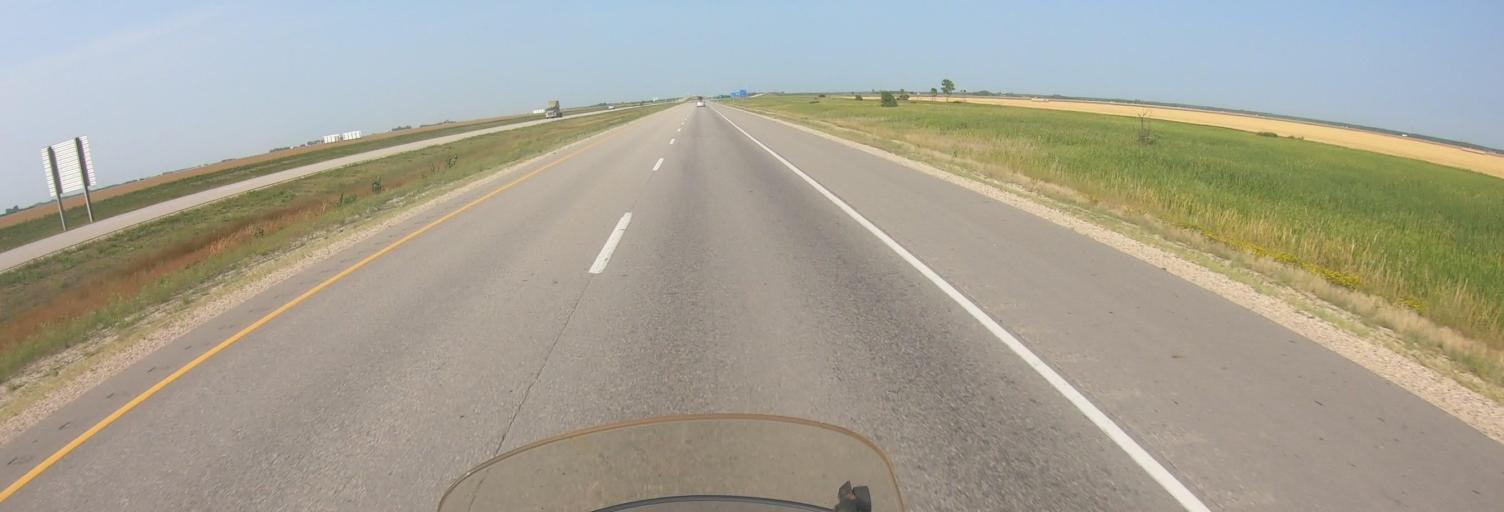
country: CA
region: Manitoba
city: Steinbach
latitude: 49.6869
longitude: -96.6563
